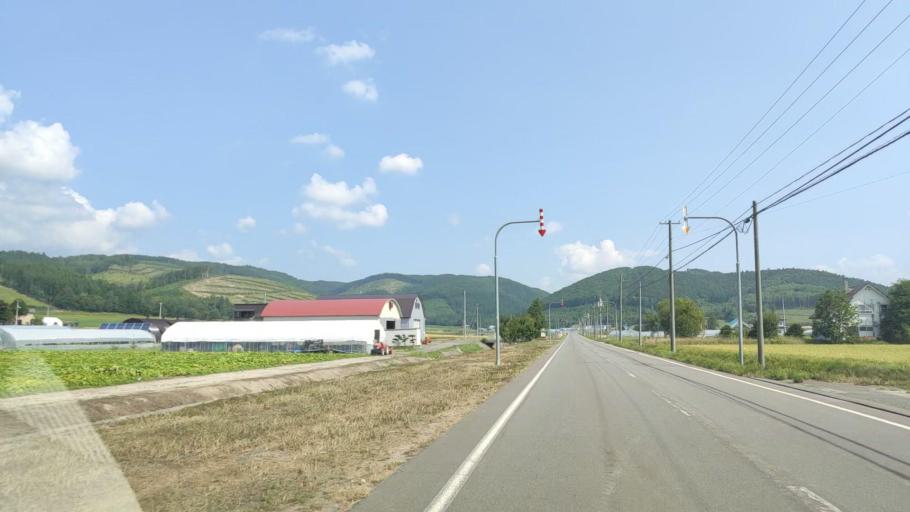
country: JP
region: Hokkaido
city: Shimo-furano
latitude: 43.4113
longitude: 142.3980
